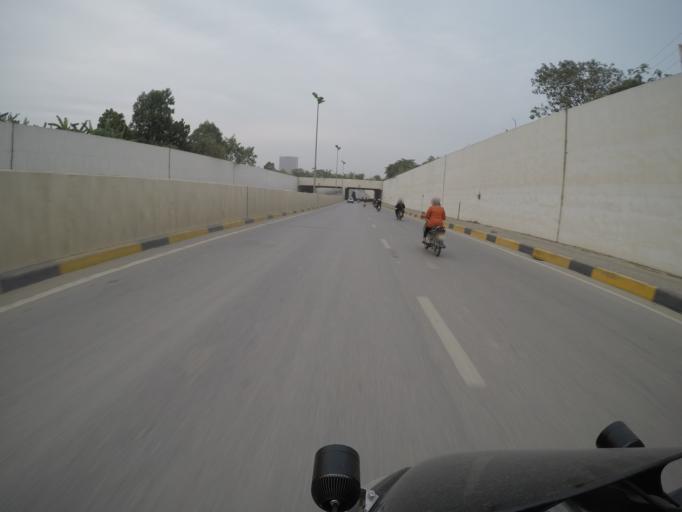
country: VN
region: Ha Noi
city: Cau Dien
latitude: 21.0101
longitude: 105.7418
